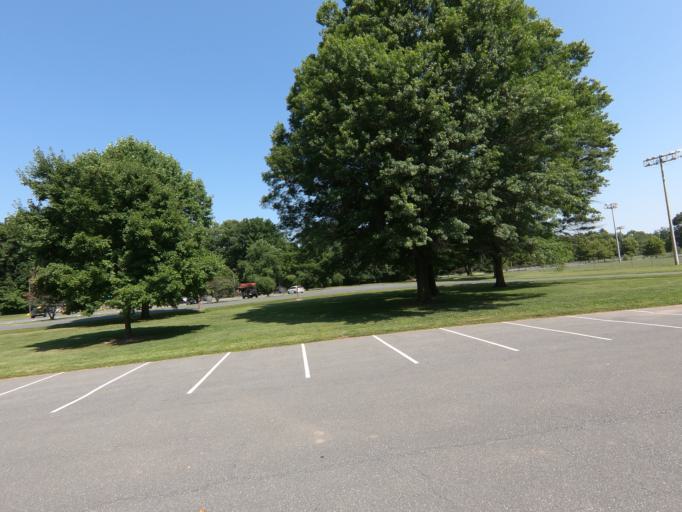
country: US
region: Maryland
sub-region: Frederick County
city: Bartonsville
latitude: 39.3882
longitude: -77.3774
